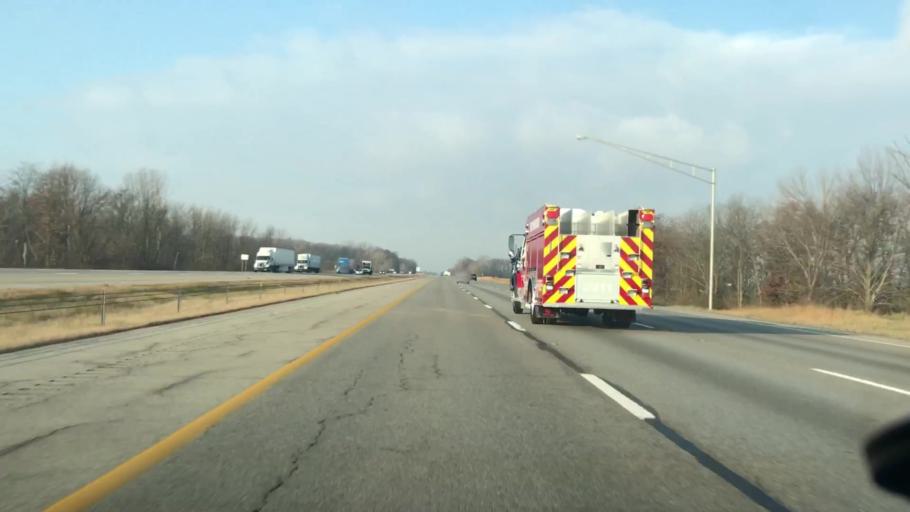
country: US
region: Ohio
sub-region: Madison County
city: Choctaw Lake
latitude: 39.9404
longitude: -83.5406
